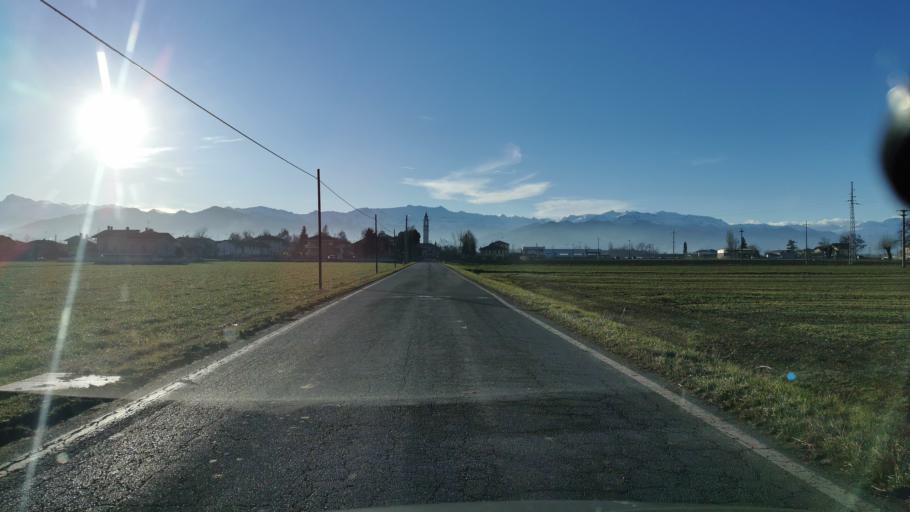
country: IT
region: Piedmont
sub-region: Provincia di Cuneo
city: Roata Rossi
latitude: 44.4557
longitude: 7.4965
